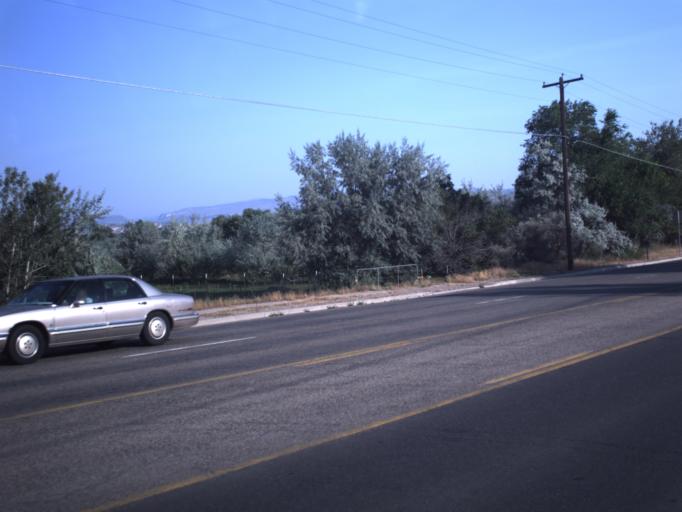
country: US
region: Utah
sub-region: Uintah County
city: Vernal
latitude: 40.4674
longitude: -109.5287
